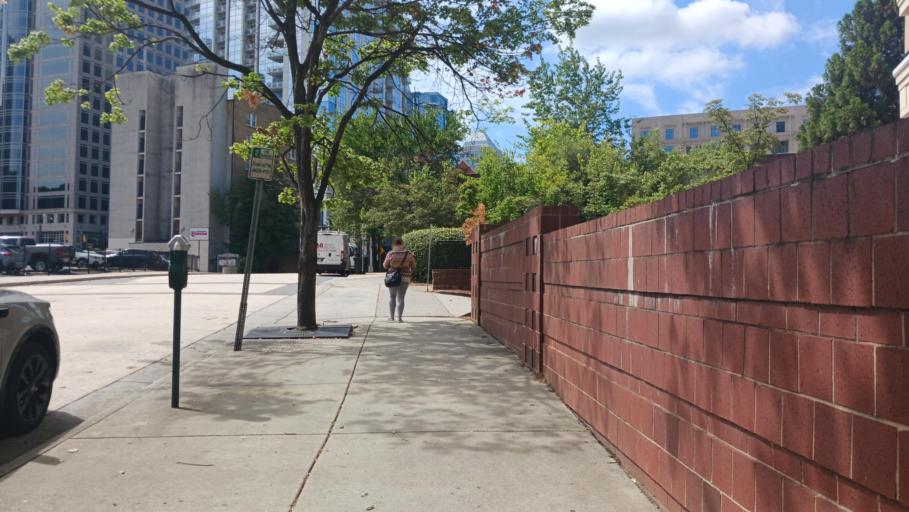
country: US
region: North Carolina
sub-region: Mecklenburg County
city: Charlotte
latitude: 35.2307
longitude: -80.8454
